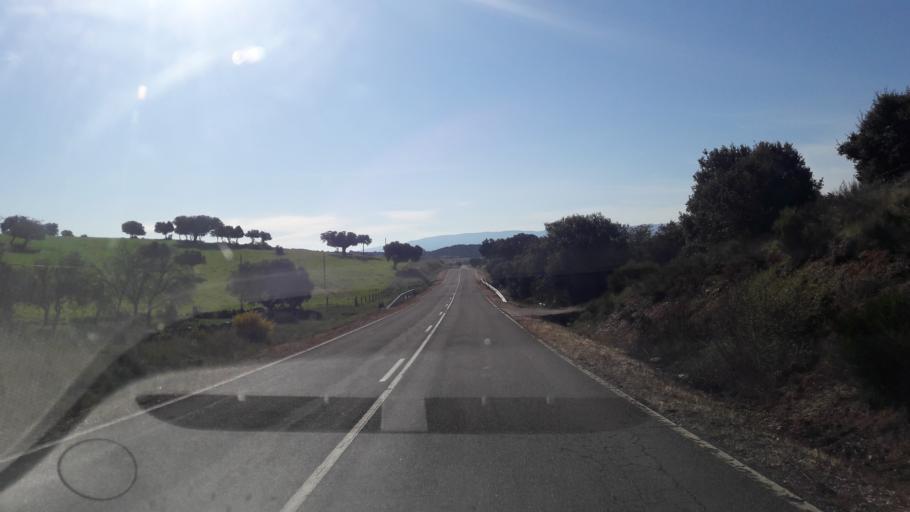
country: ES
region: Castille and Leon
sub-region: Provincia de Salamanca
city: Puente del Congosto
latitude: 40.5279
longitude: -5.5144
